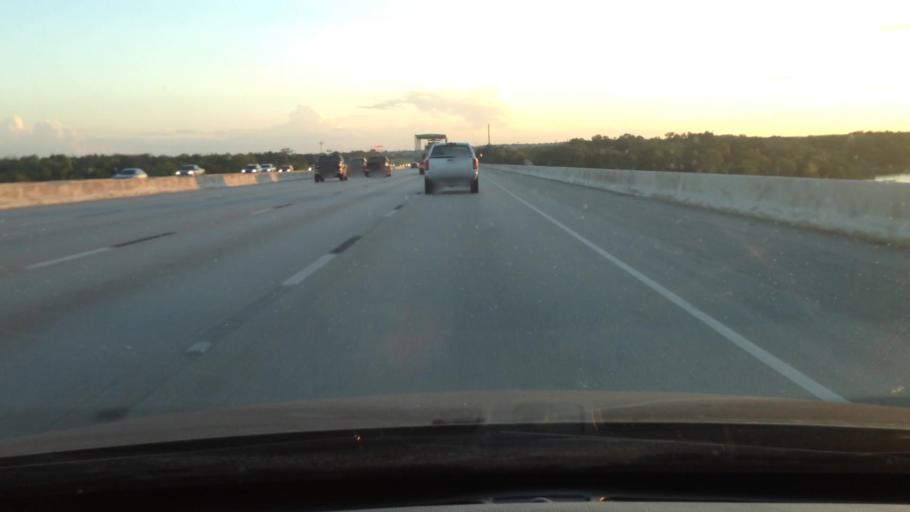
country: US
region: Texas
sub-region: Tarrant County
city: Lake Worth
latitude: 32.7925
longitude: -97.4556
